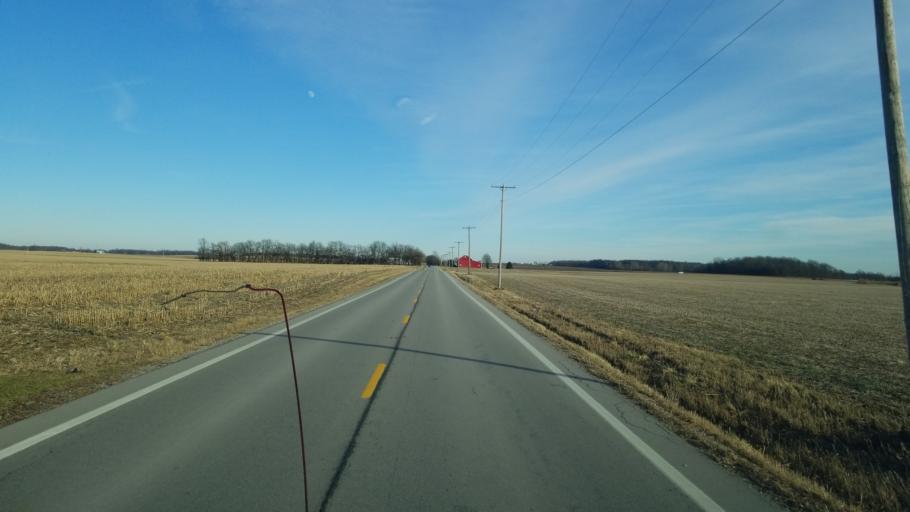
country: US
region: Ohio
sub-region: Huron County
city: Greenwich
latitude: 41.1039
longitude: -82.5956
